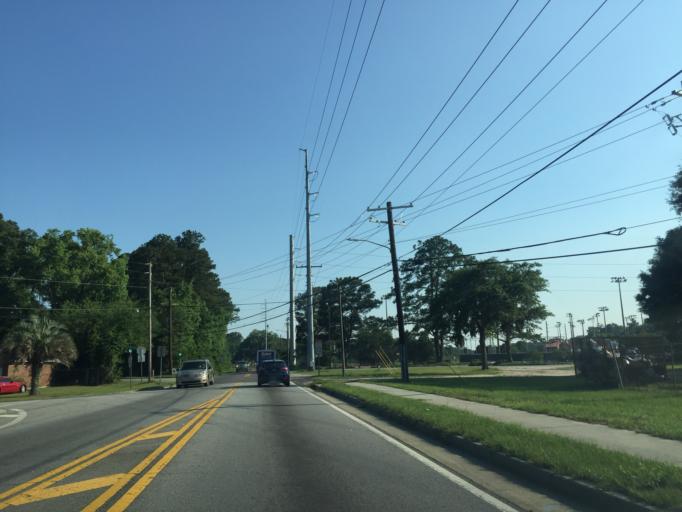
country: US
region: Georgia
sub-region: Chatham County
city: Isle of Hope
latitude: 31.9978
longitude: -81.0780
